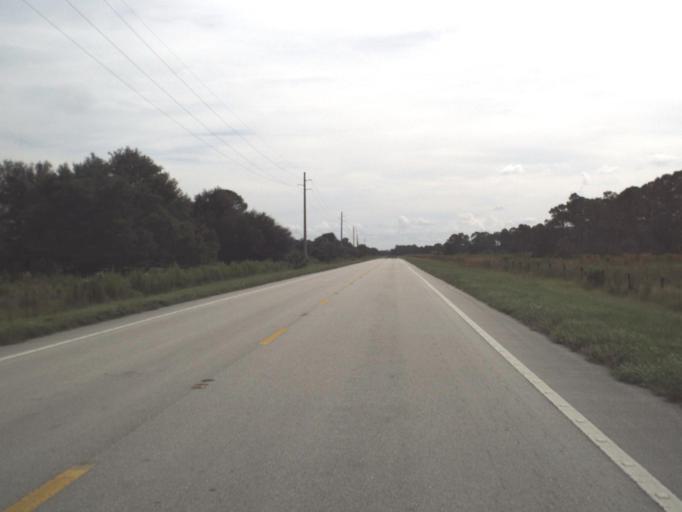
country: US
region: Florida
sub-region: Highlands County
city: Placid Lakes
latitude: 27.2088
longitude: -81.4855
